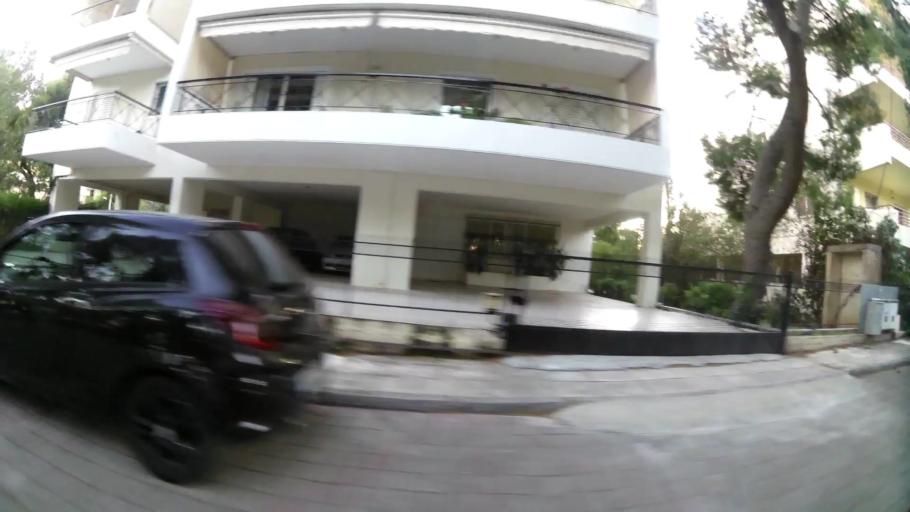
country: GR
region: Attica
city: Pefki
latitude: 38.0603
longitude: 23.7901
